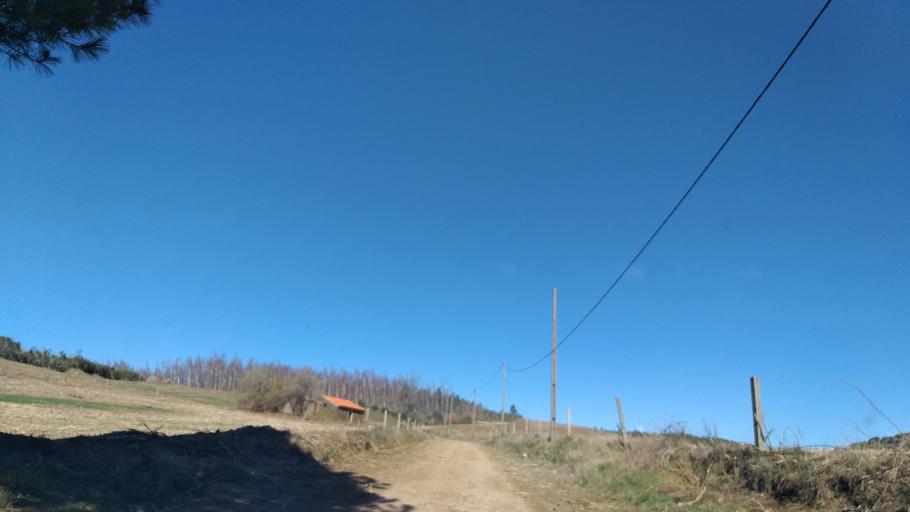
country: PT
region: Guarda
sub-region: Celorico da Beira
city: Celorico da Beira
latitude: 40.5140
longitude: -7.4555
